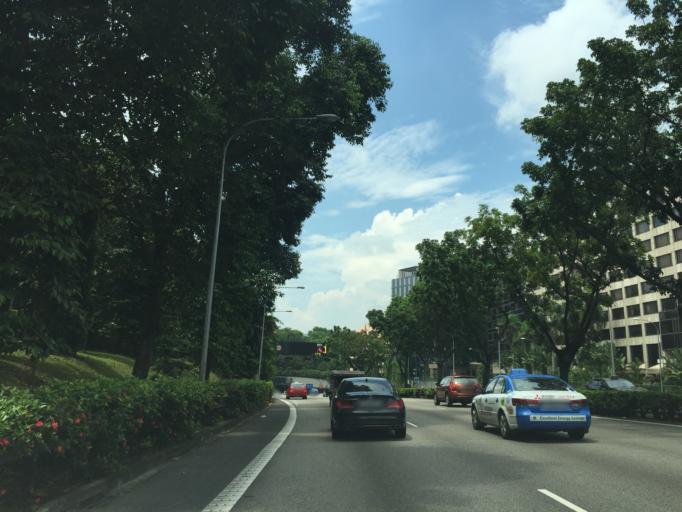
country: SG
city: Singapore
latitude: 1.3033
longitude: 103.8409
